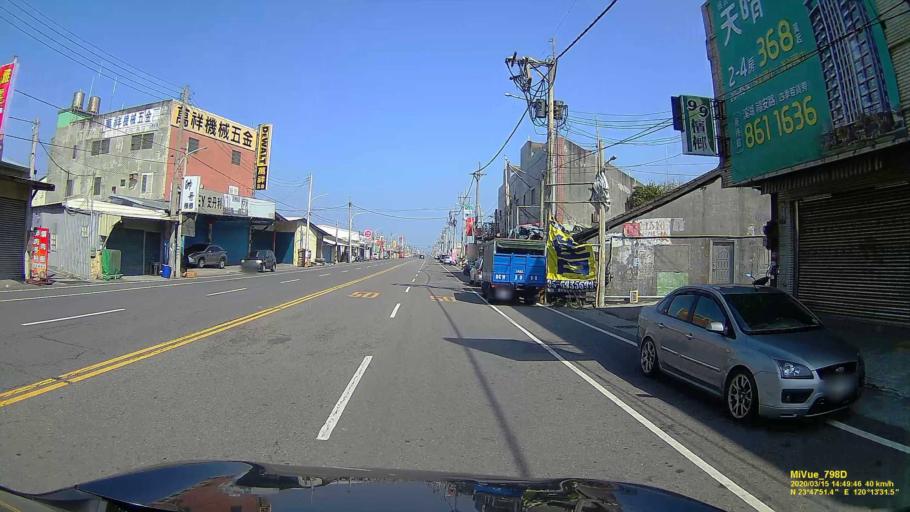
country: TW
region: Taiwan
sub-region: Yunlin
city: Douliu
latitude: 23.7976
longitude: 120.2256
